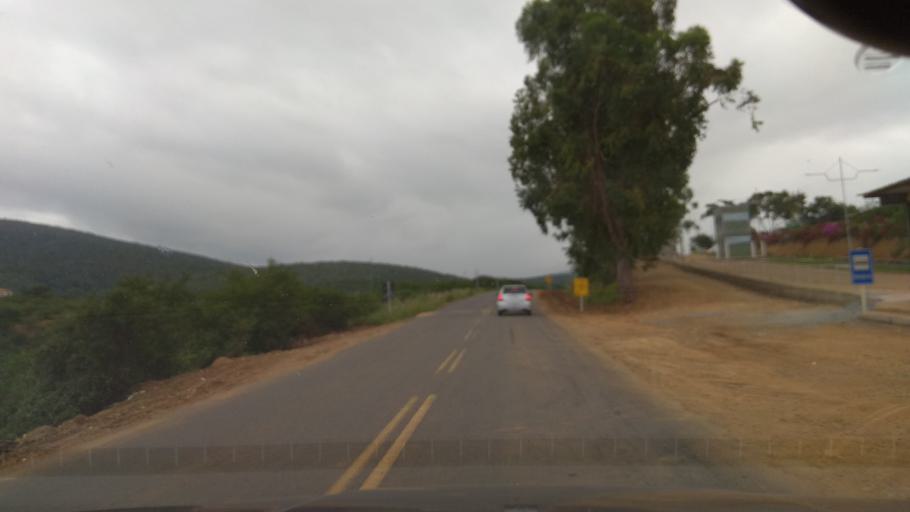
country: BR
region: Bahia
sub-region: Santa Ines
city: Santa Ines
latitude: -13.2730
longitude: -39.8064
